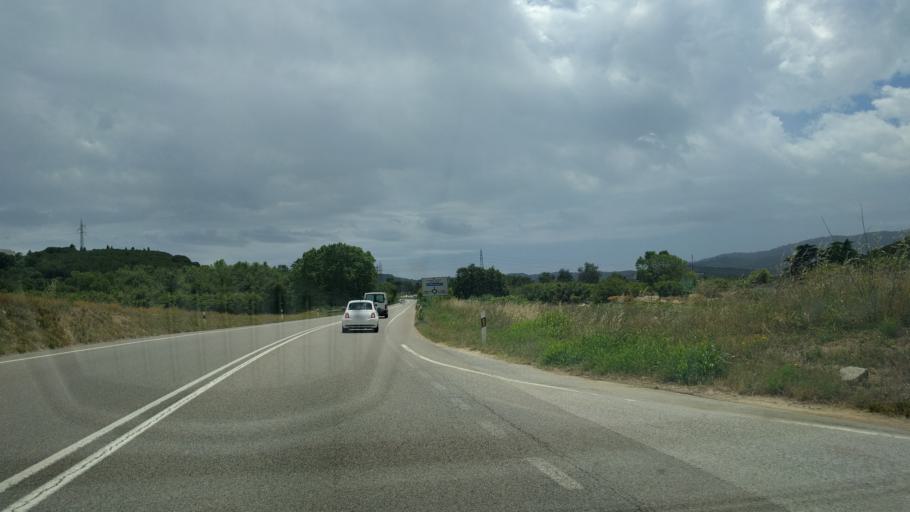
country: ES
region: Catalonia
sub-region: Provincia de Barcelona
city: Tordera
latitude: 41.7086
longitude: 2.7310
